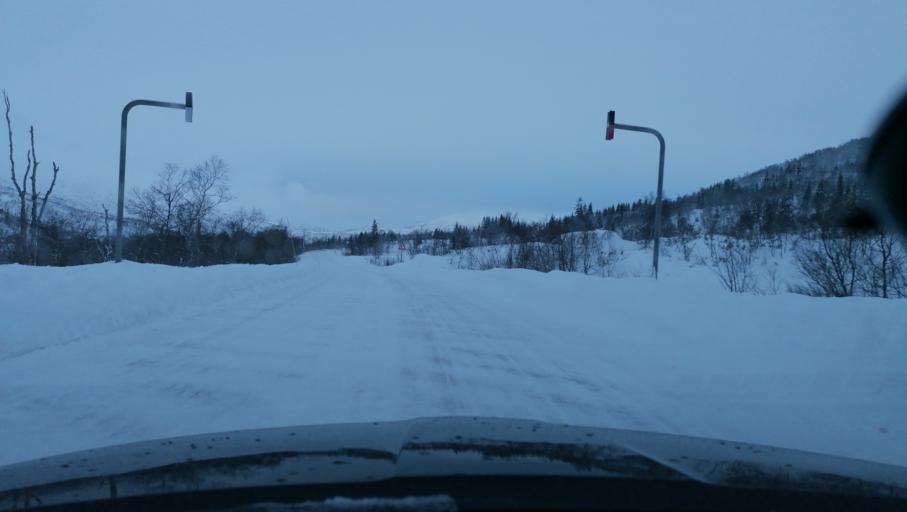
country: NO
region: Aust-Agder
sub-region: Bykle
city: Hovden
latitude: 59.6362
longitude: 7.4539
